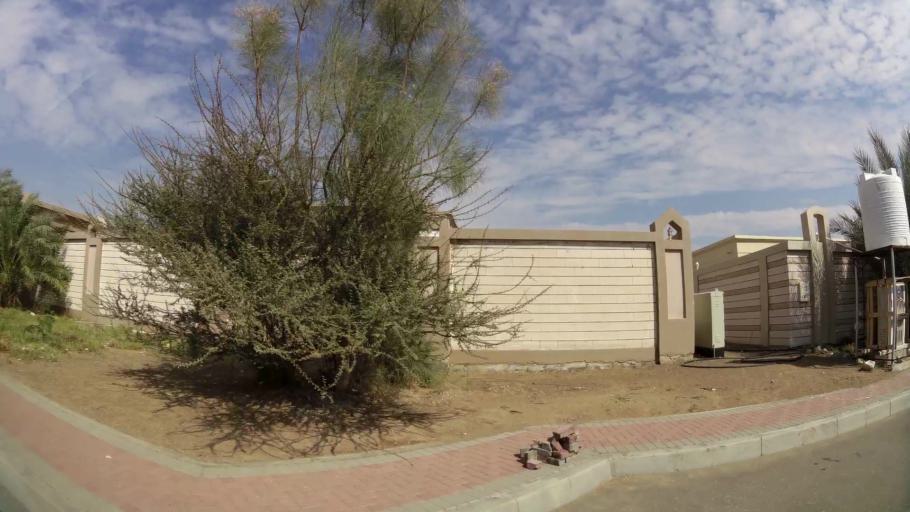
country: AE
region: Abu Dhabi
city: Al Ain
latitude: 24.0987
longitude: 55.9122
